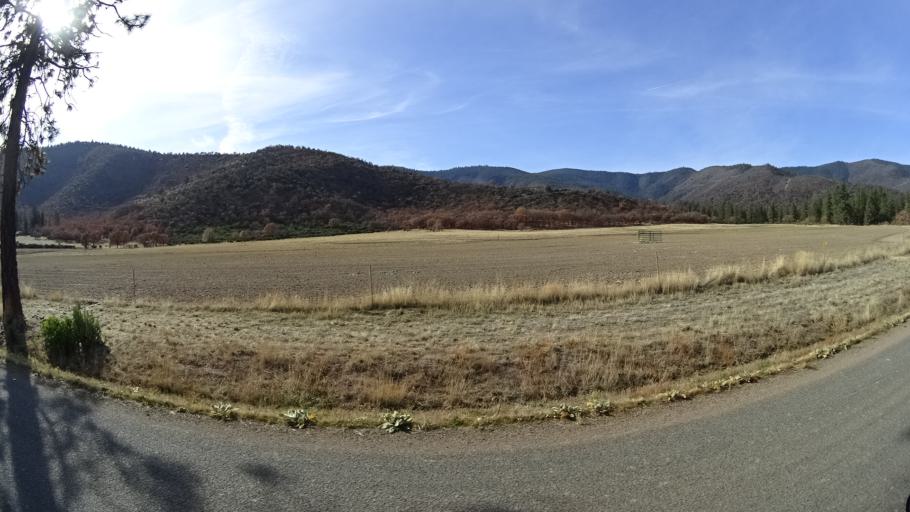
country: US
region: California
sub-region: Siskiyou County
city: Montague
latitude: 41.5406
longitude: -122.5881
